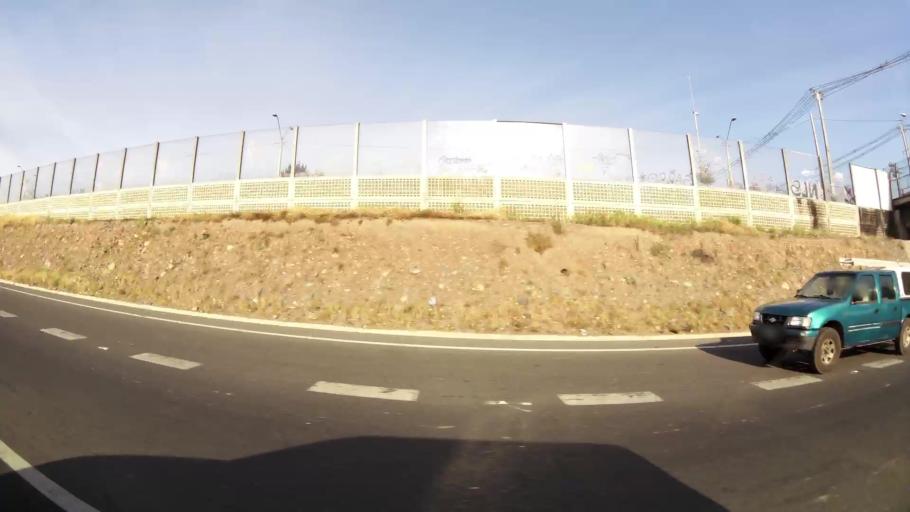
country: CL
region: Santiago Metropolitan
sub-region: Provincia de Santiago
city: La Pintana
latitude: -33.5858
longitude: -70.6103
